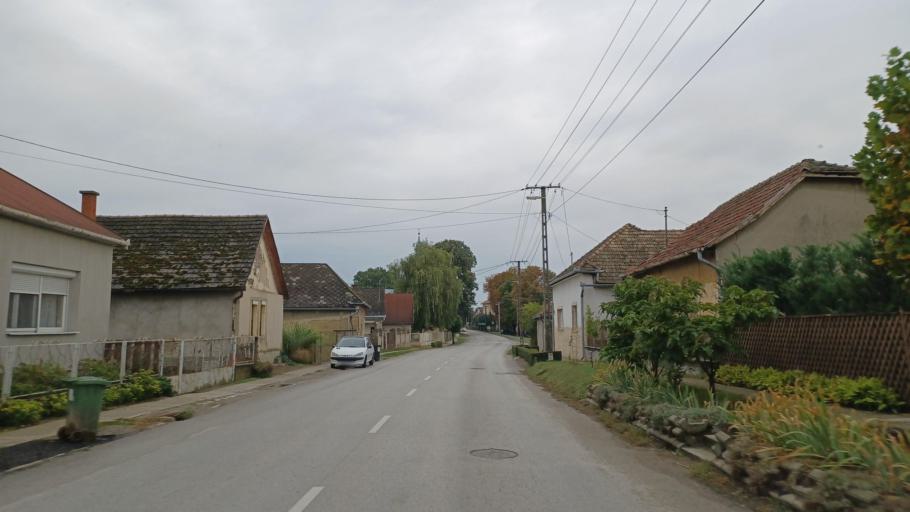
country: HU
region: Tolna
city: Nagydorog
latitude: 46.6312
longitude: 18.6550
